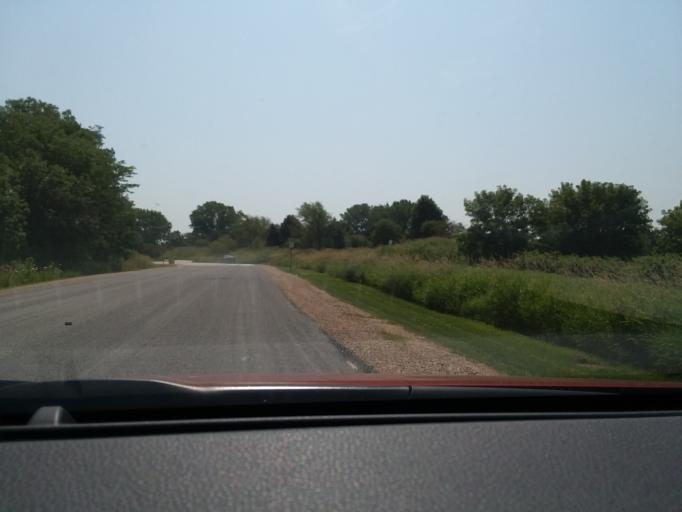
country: US
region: Wisconsin
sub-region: Dane County
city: McFarland
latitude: 43.0441
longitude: -89.2636
